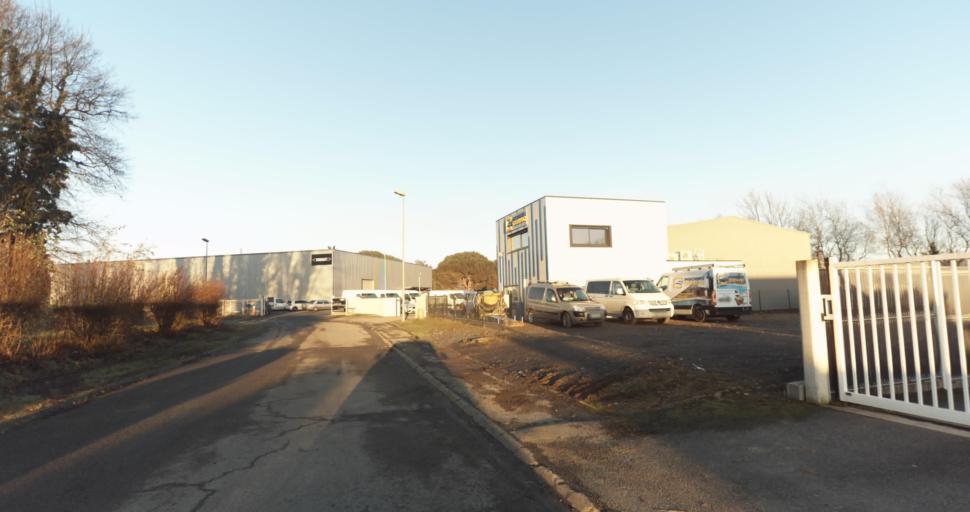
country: FR
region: Aquitaine
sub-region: Departement des Pyrenees-Atlantiques
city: Buros
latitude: 43.3241
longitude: -0.2941
